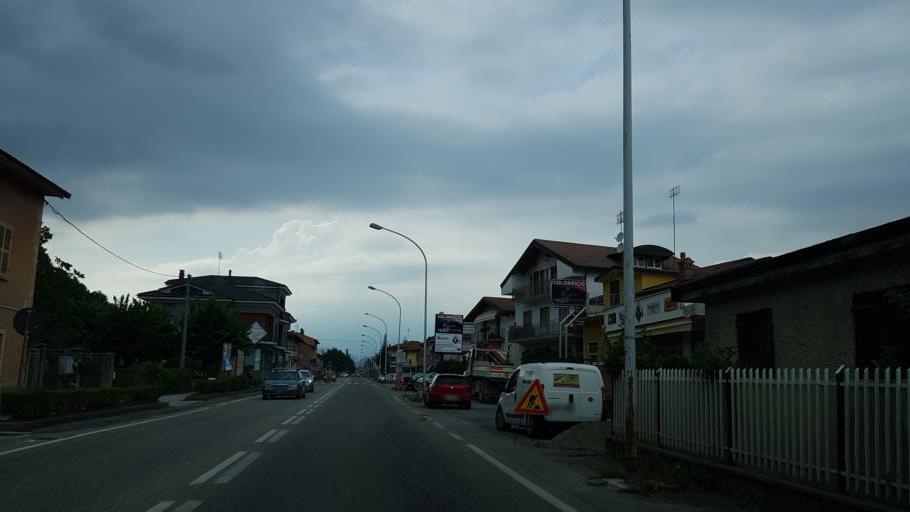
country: IT
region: Piedmont
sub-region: Provincia di Cuneo
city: Borgo San Dalmazzo
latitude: 44.3311
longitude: 7.4802
